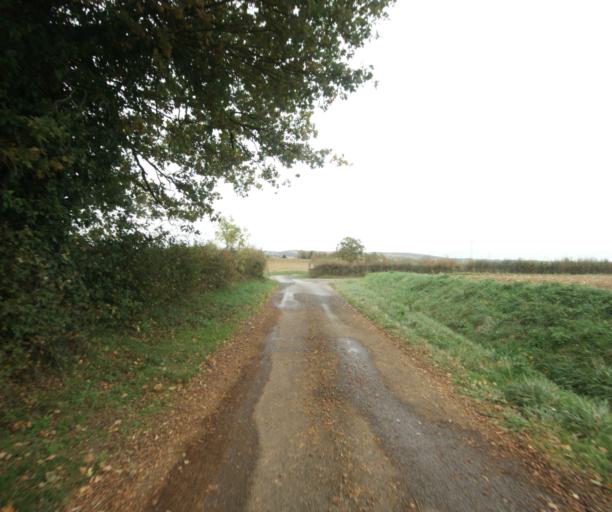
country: FR
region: Rhone-Alpes
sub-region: Departement de l'Ain
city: Pont-de-Vaux
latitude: 46.4672
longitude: 4.8724
